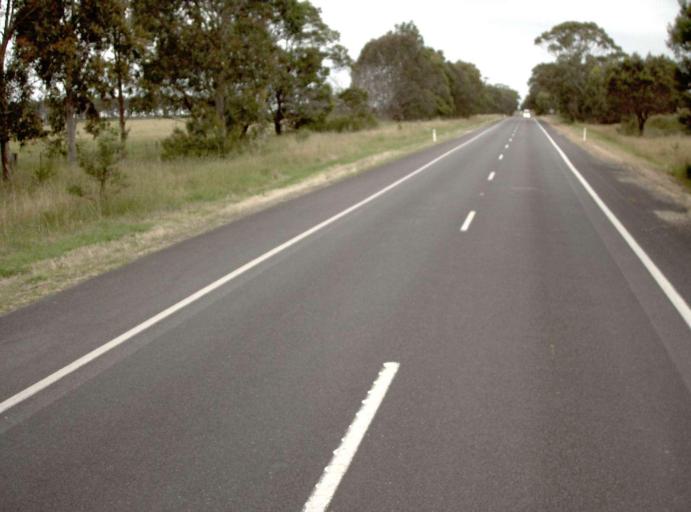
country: AU
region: Victoria
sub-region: Wellington
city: Sale
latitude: -38.2988
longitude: 147.0334
